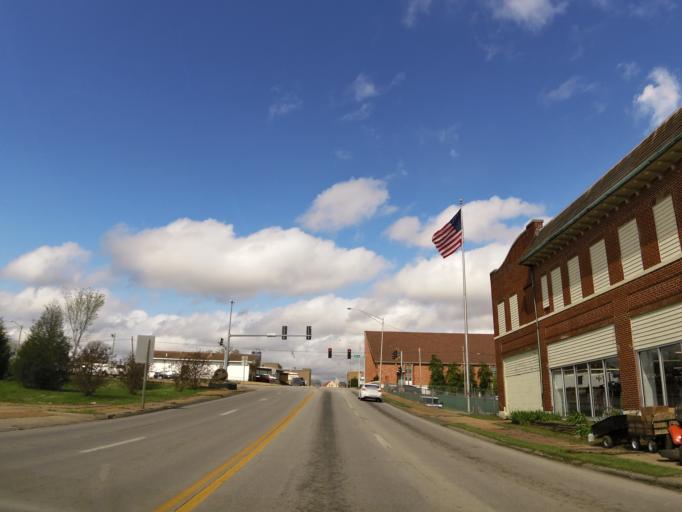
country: US
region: Missouri
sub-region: Butler County
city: Poplar Bluff
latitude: 36.7572
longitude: -90.3944
